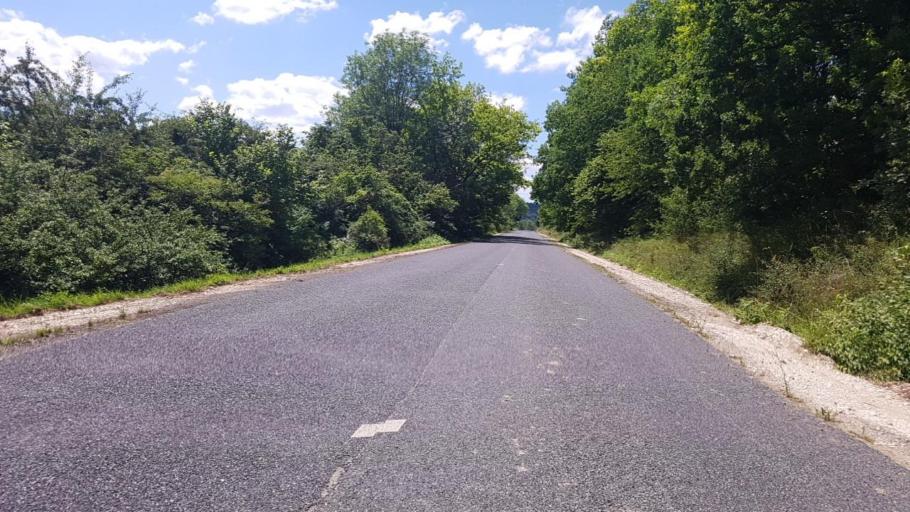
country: FR
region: Lorraine
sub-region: Departement de la Meuse
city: Ligny-en-Barrois
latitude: 48.6425
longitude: 5.3913
